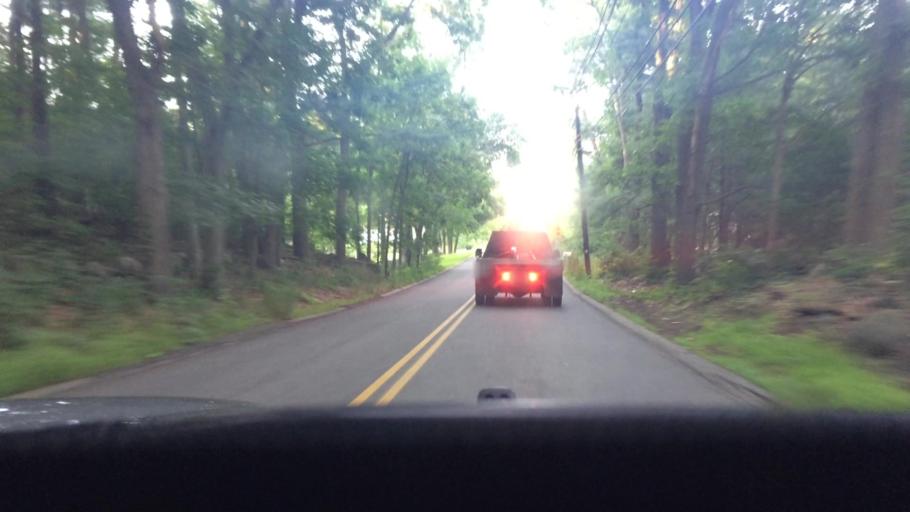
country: US
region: Massachusetts
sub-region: Middlesex County
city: North Reading
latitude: 42.6250
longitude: -71.0937
